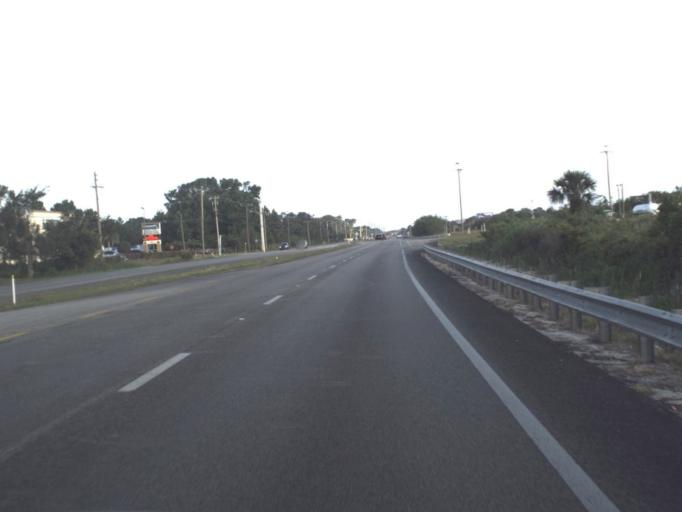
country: US
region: Florida
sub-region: Brevard County
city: Rockledge
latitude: 28.2754
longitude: -80.6934
